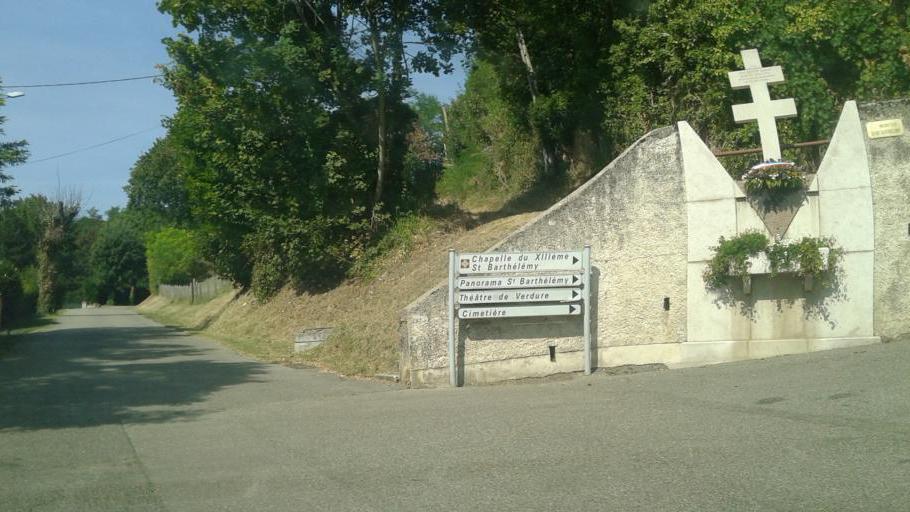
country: FR
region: Rhone-Alpes
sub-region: Departement de l'Ain
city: Montluel
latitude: 45.8523
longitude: 5.0502
